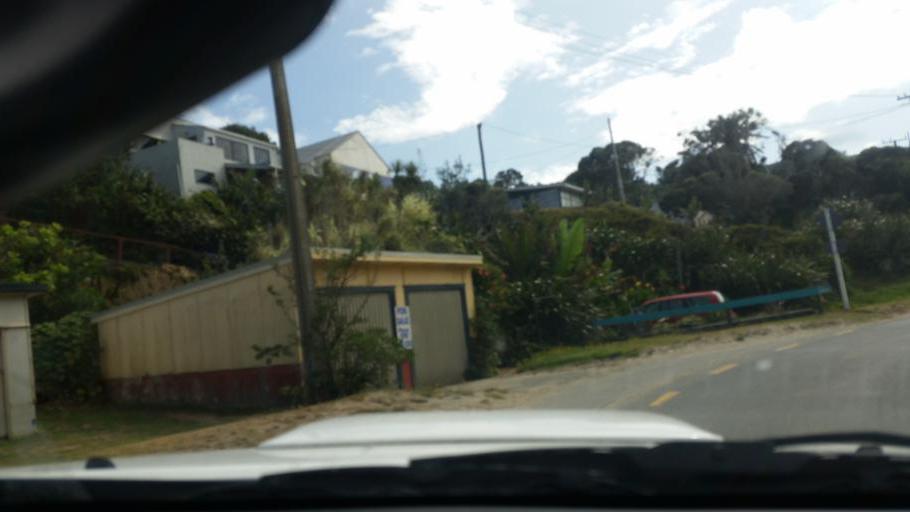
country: NZ
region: Northland
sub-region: Kaipara District
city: Dargaville
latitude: -35.9496
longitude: 173.7432
